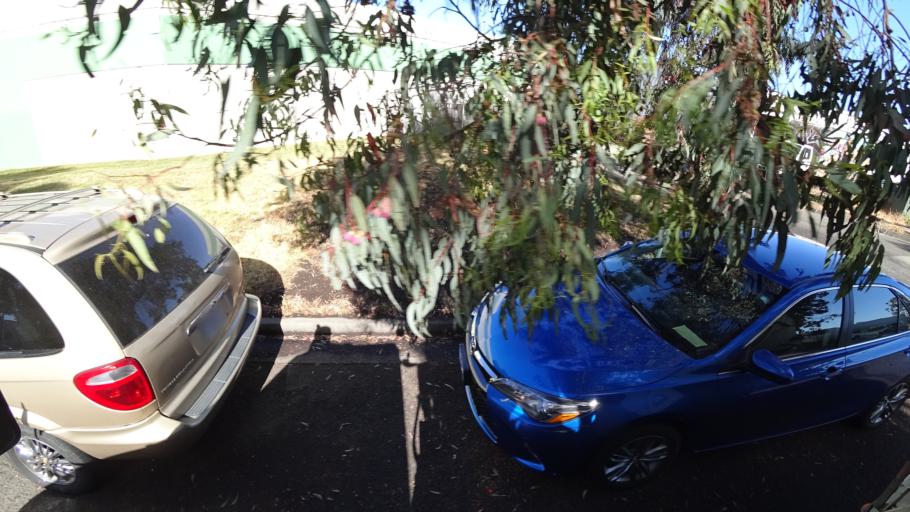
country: US
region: California
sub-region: Alameda County
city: San Lorenzo
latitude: 37.6407
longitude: -122.1332
